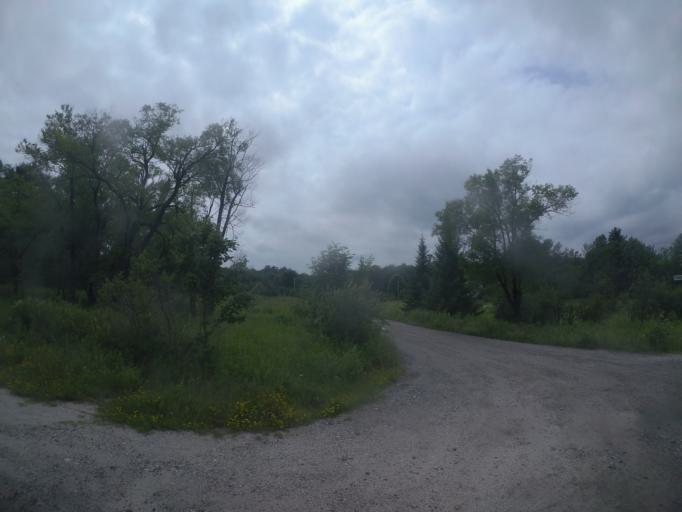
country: US
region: Maine
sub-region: Cumberland County
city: Cumberland Center
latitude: 43.7659
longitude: -70.2466
